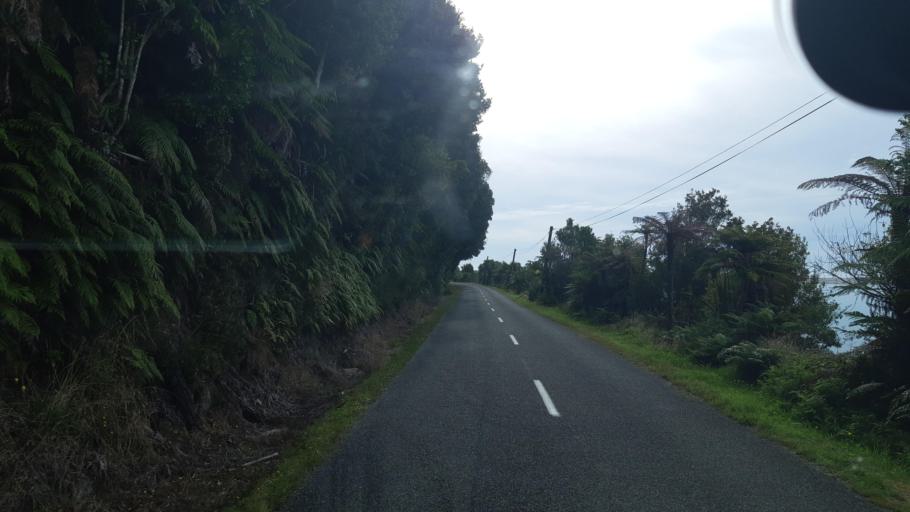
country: NZ
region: West Coast
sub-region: Westland District
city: Hokitika
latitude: -43.2237
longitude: 170.1739
